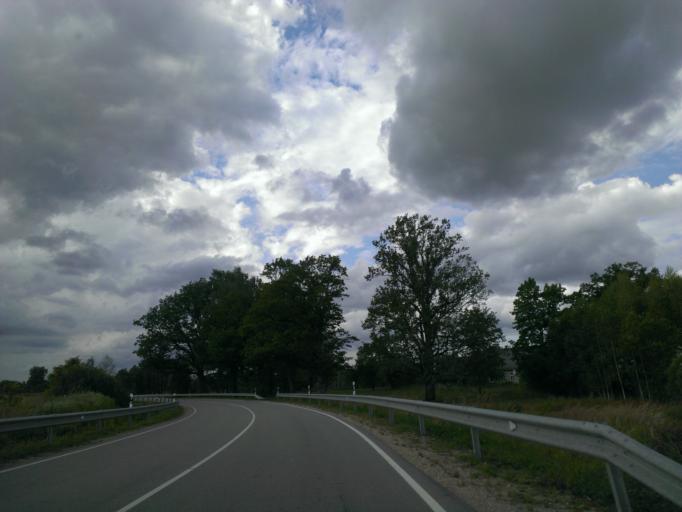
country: LV
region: Malpils
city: Malpils
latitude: 56.8941
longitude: 25.1546
